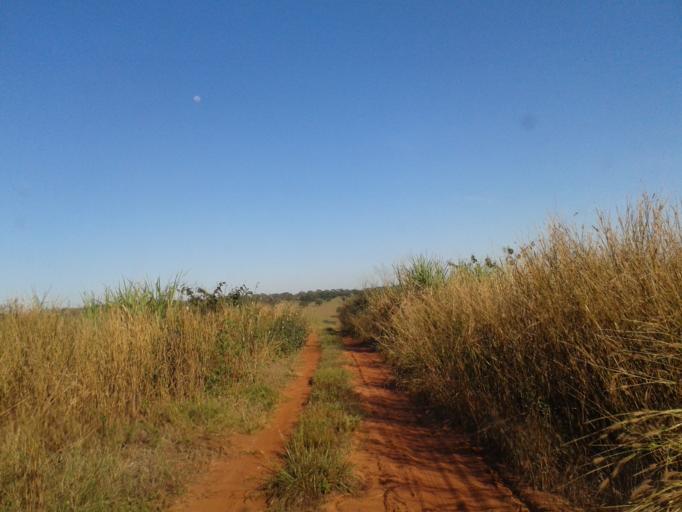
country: BR
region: Minas Gerais
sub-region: Santa Vitoria
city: Santa Vitoria
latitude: -19.0197
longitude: -50.3754
